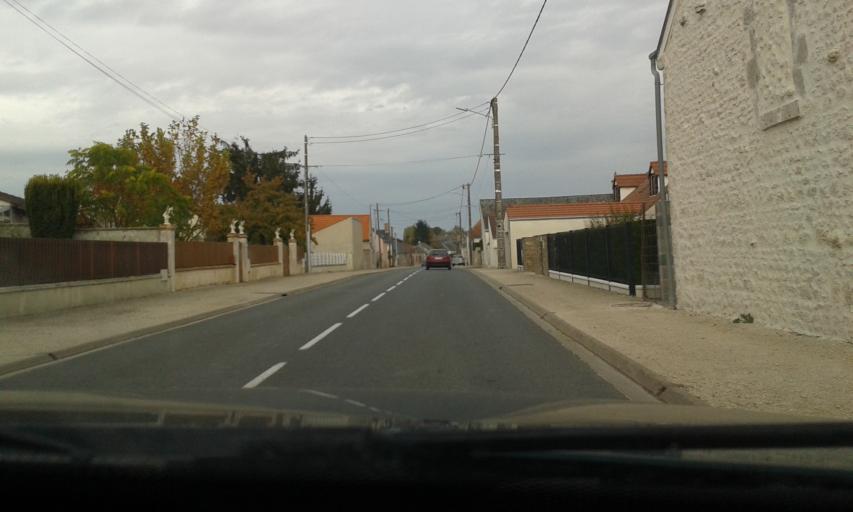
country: FR
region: Centre
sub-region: Departement du Loiret
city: Gidy
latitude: 47.9858
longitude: 1.8382
